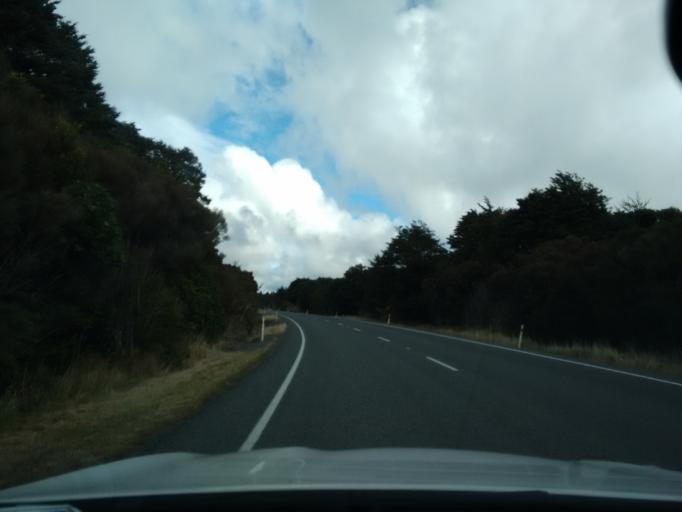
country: NZ
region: Manawatu-Wanganui
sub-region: Ruapehu District
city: Waiouru
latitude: -39.3001
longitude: 175.3884
